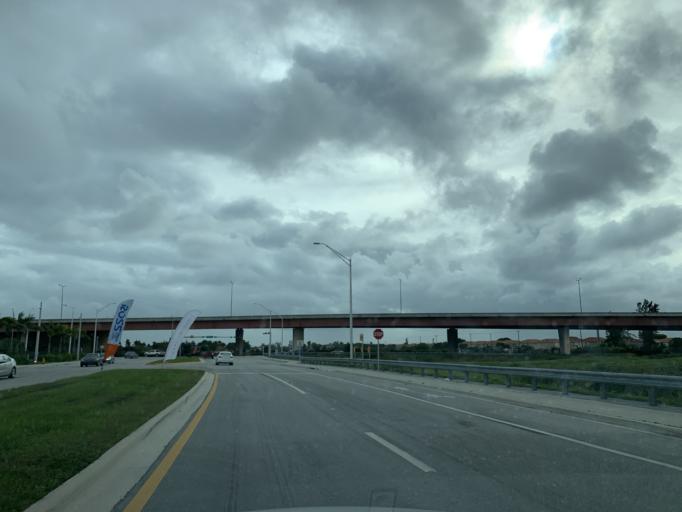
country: US
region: Florida
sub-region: Miami-Dade County
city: Tamiami
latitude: 25.7841
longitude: -80.3909
